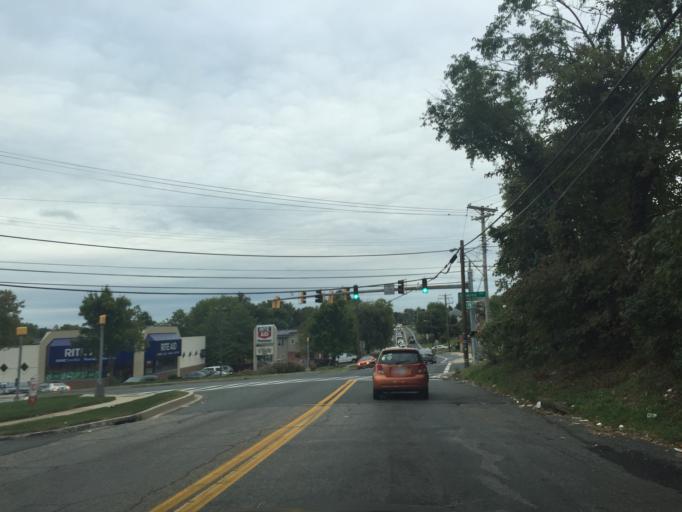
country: US
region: Maryland
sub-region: Baltimore County
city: Rosedale
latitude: 39.3379
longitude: -76.5055
